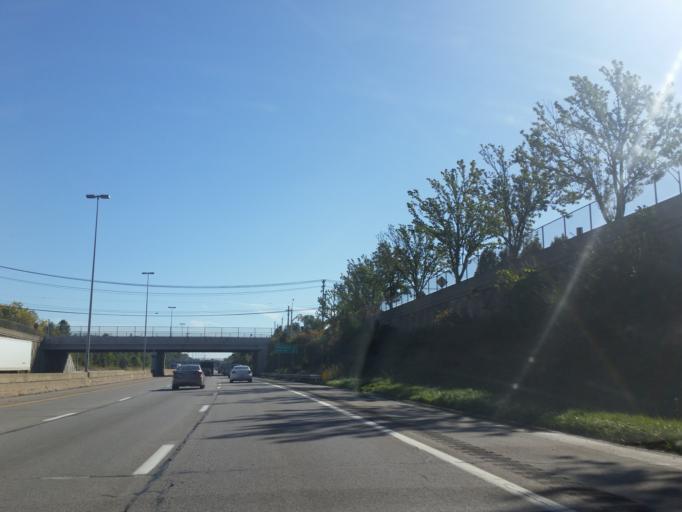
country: US
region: Ohio
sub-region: Cuyahoga County
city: Rocky River
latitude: 41.4720
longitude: -81.8541
